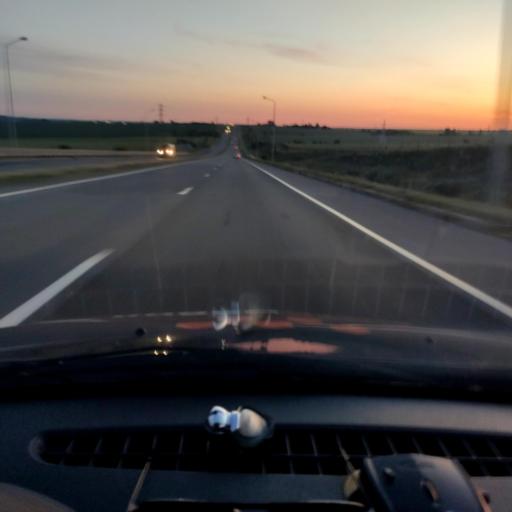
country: RU
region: Belgorod
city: Staryy Oskol
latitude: 51.3252
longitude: 37.7310
